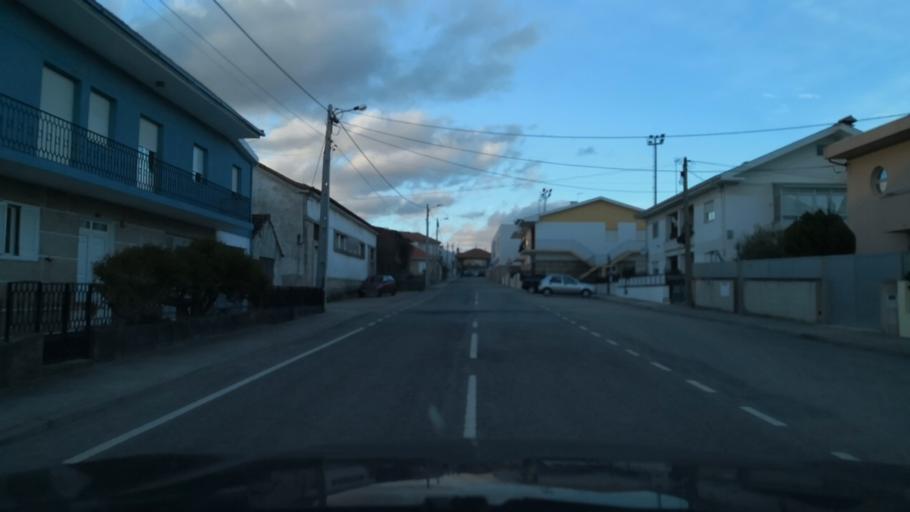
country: PT
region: Braganca
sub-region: Carrazeda de Ansiaes
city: Carrazeda de Anciaes
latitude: 41.2370
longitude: -7.3063
